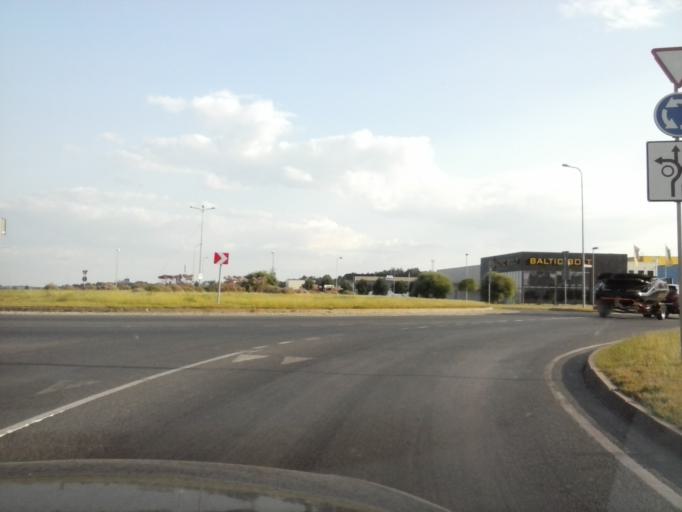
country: EE
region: Tartu
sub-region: UElenurme vald
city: Ulenurme
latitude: 58.3434
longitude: 26.7410
